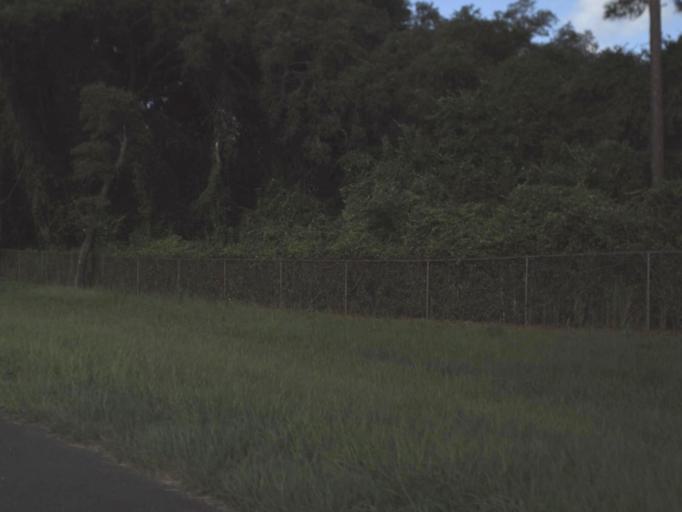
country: US
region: Florida
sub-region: Hernando County
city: Masaryktown
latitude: 28.4089
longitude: -82.4756
